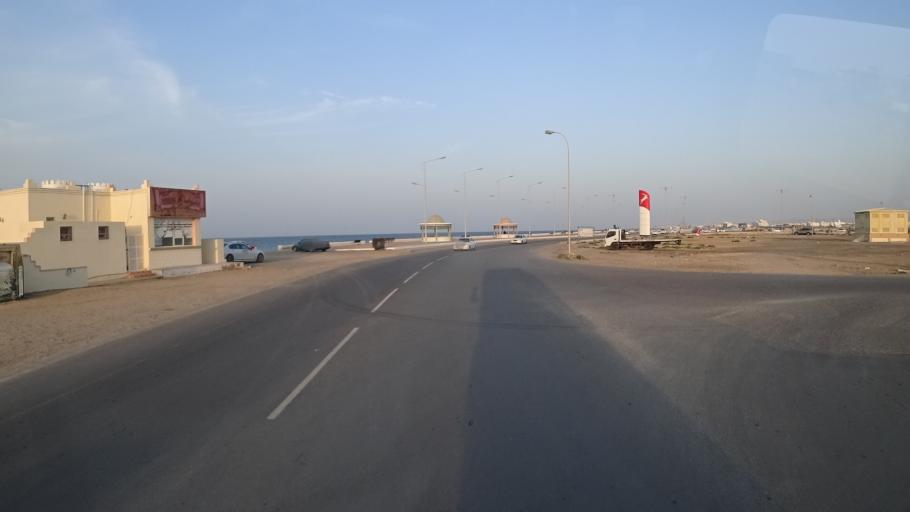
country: OM
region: Ash Sharqiyah
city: Sur
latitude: 22.6038
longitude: 59.4813
